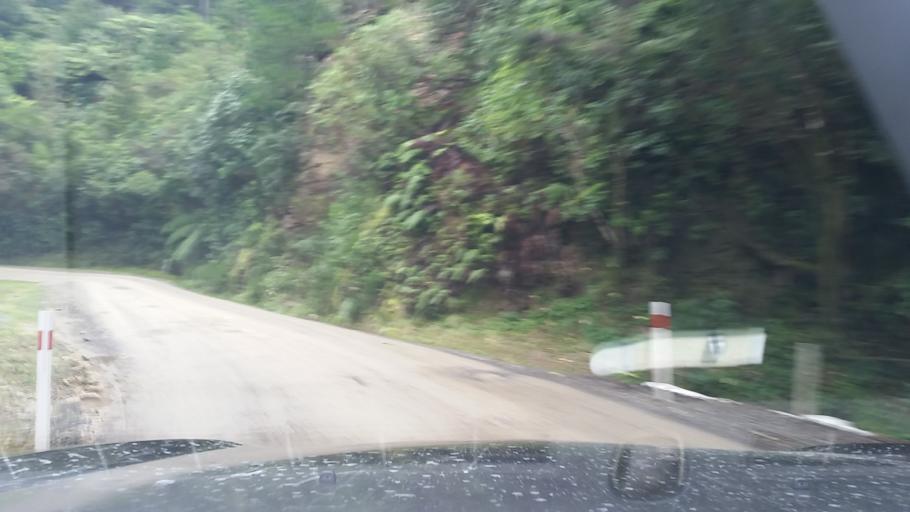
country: NZ
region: Marlborough
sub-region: Marlborough District
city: Picton
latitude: -41.1759
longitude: 174.0774
